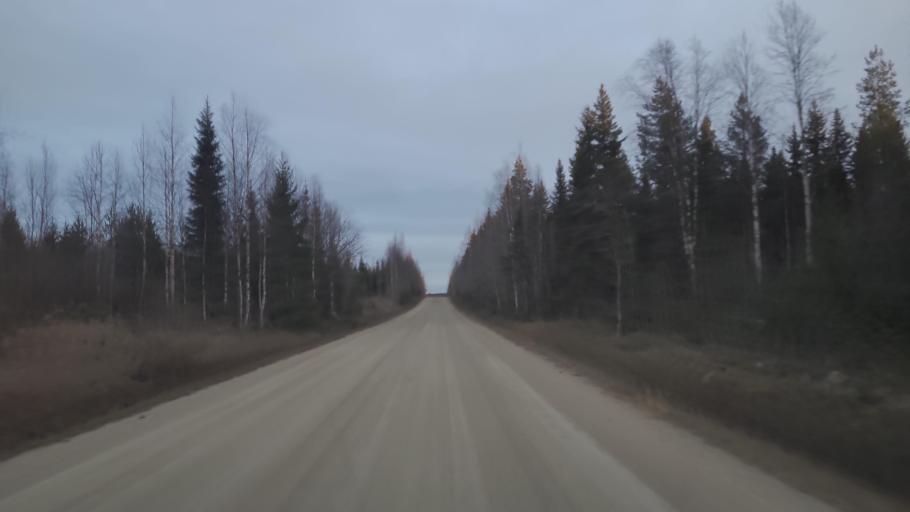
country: FI
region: Lapland
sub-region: Kemi-Tornio
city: Tervola
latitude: 66.0584
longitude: 24.9418
